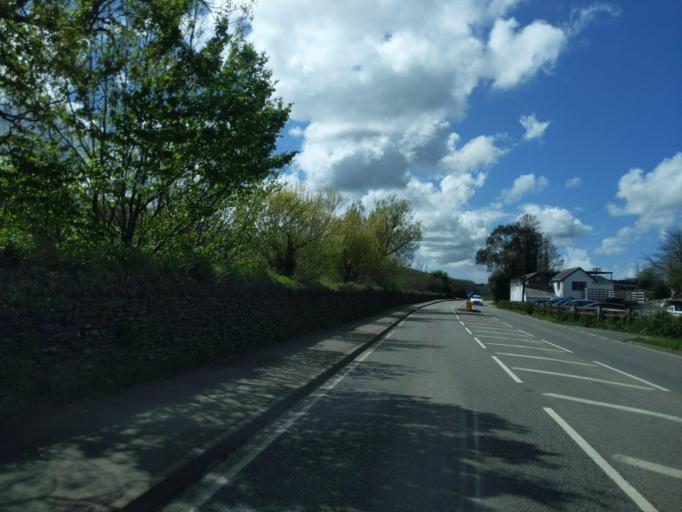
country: GB
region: England
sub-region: Cornwall
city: Wadebridge
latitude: 50.5091
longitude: -4.8083
